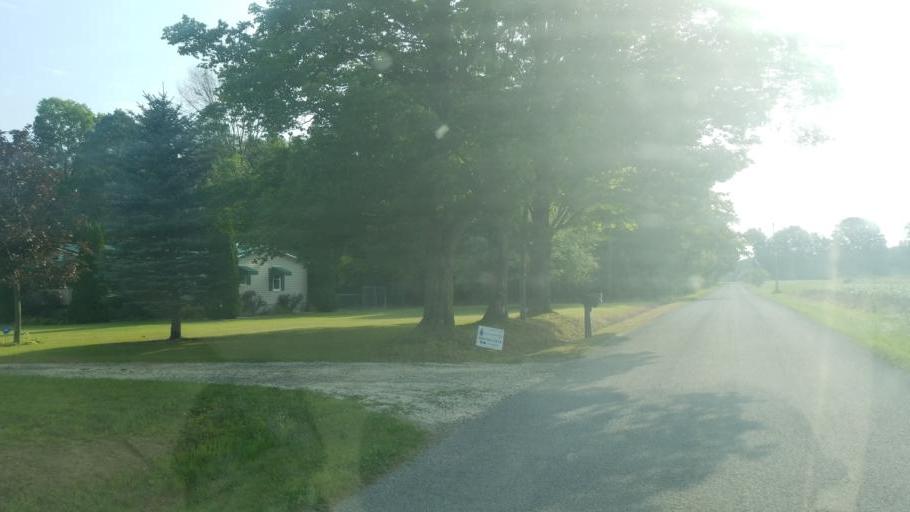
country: US
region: Pennsylvania
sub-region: Crawford County
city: Pymatuning Central
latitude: 41.6260
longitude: -80.4881
